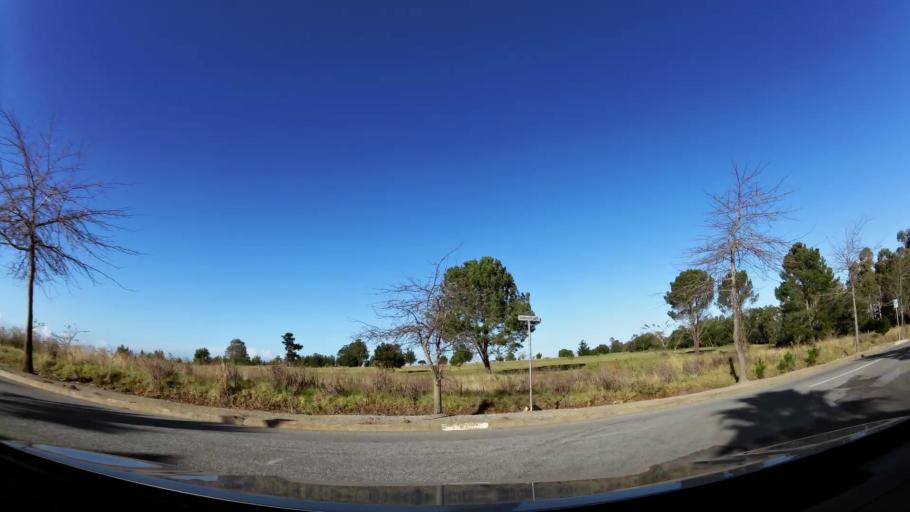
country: ZA
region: Western Cape
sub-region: Eden District Municipality
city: George
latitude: -33.9621
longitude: 22.4419
